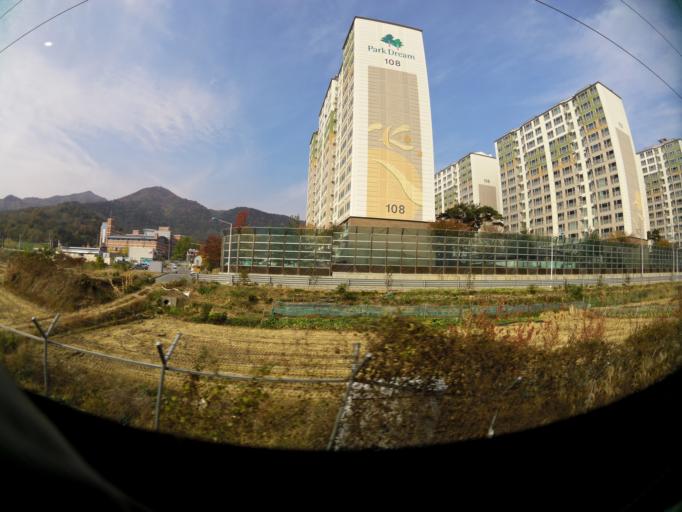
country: KR
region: Gyeongsangbuk-do
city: Gumi
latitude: 36.0968
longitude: 128.3554
